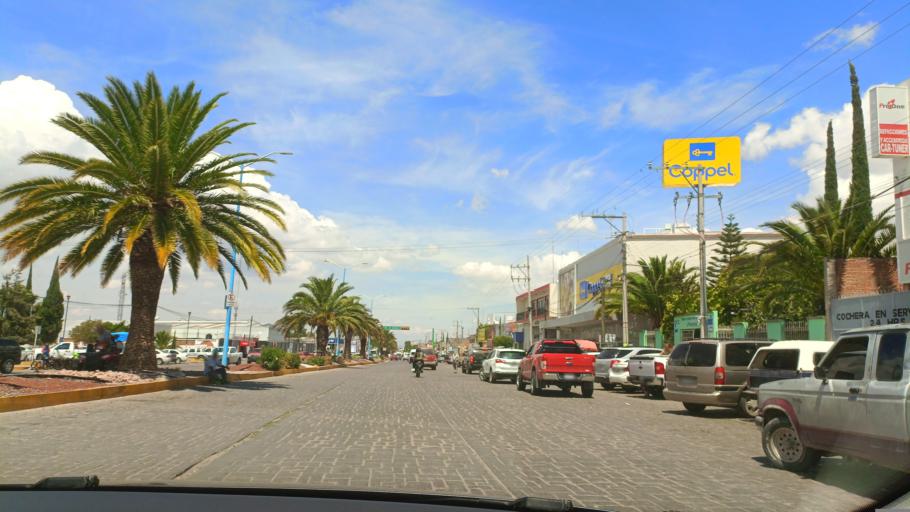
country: MX
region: Guerrero
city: San Luis de la Paz
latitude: 21.2967
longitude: -100.5247
